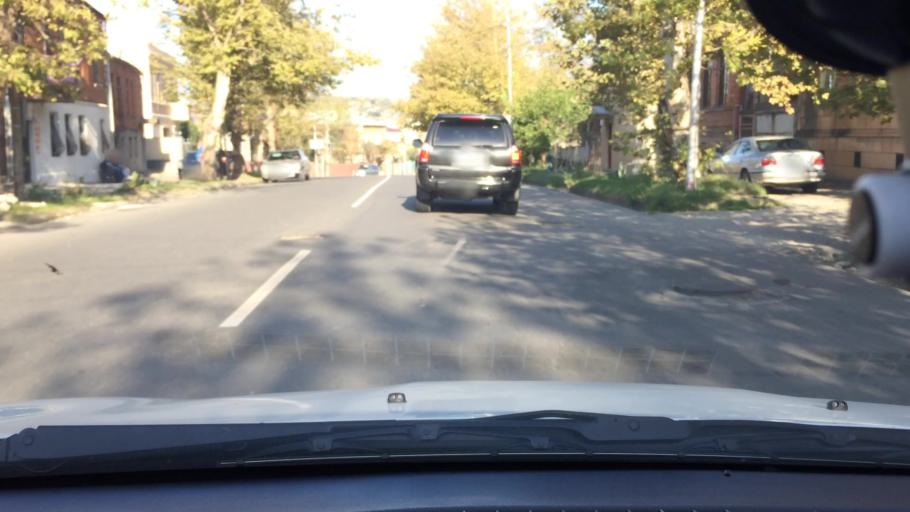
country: GE
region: Imereti
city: Kutaisi
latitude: 42.2687
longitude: 42.7155
